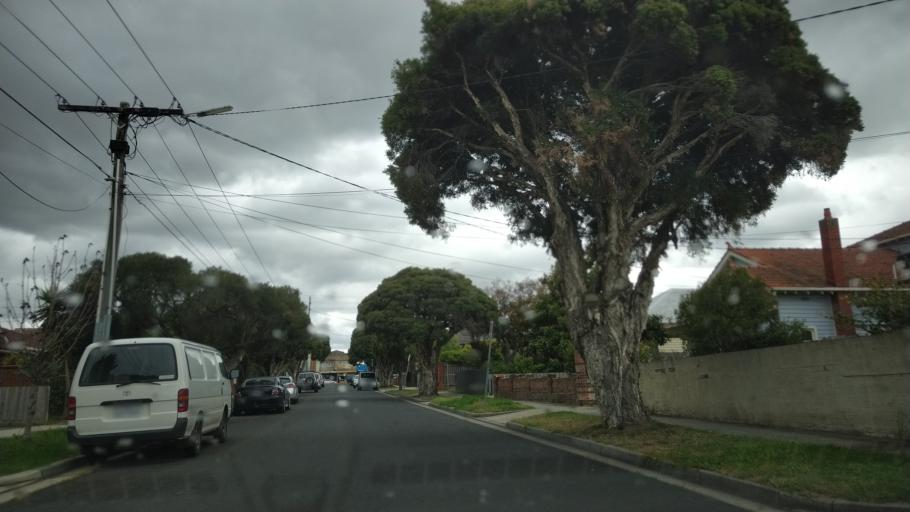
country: AU
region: Victoria
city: Ormond
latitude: -37.9056
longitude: 145.0406
